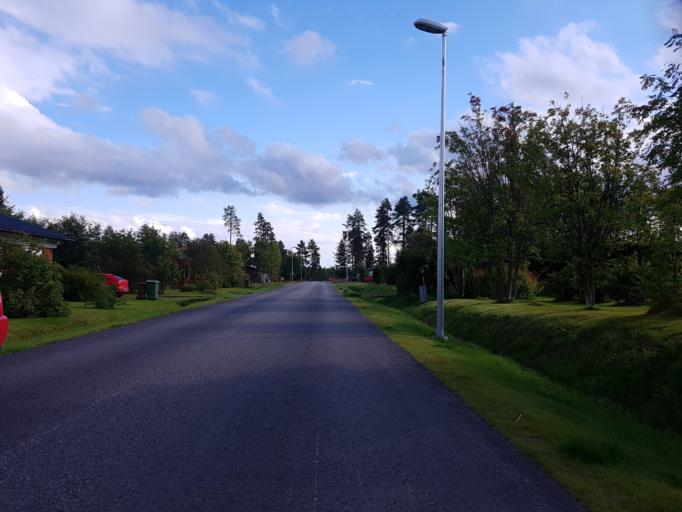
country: FI
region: Kainuu
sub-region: Kehys-Kainuu
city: Kuhmo
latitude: 64.1199
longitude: 29.5353
